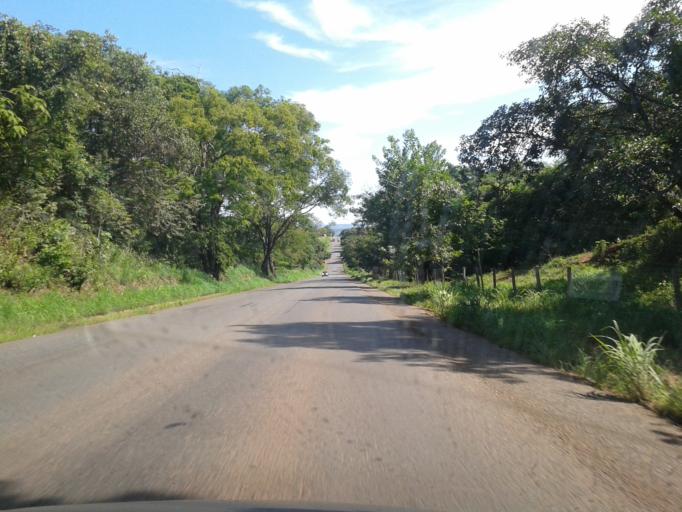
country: BR
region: Goias
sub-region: Piracanjuba
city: Piracanjuba
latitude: -17.2243
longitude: -48.7131
